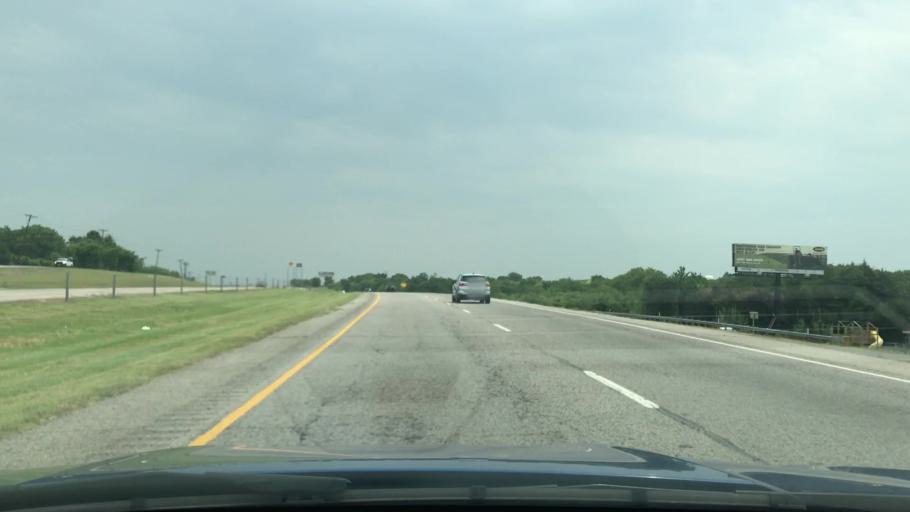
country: US
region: Texas
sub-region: Kaufman County
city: Forney
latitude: 32.7600
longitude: -96.4783
